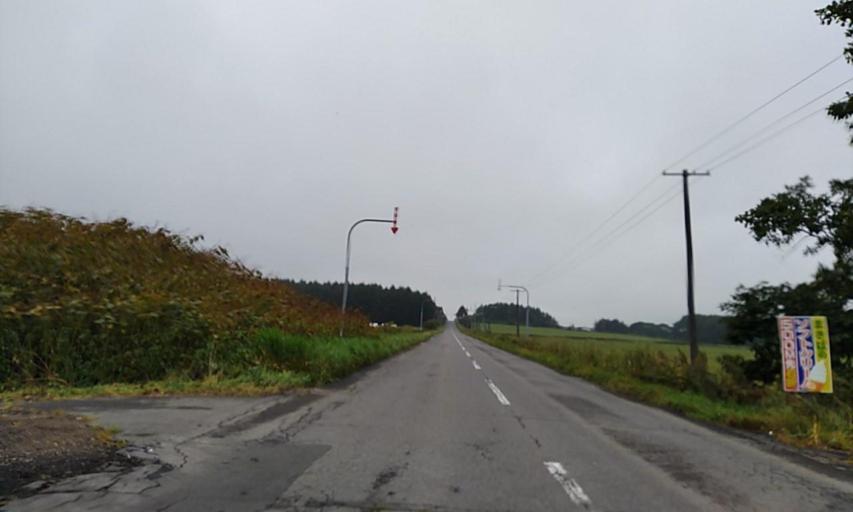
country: JP
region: Hokkaido
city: Shibetsu
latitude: 43.5097
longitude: 144.6691
